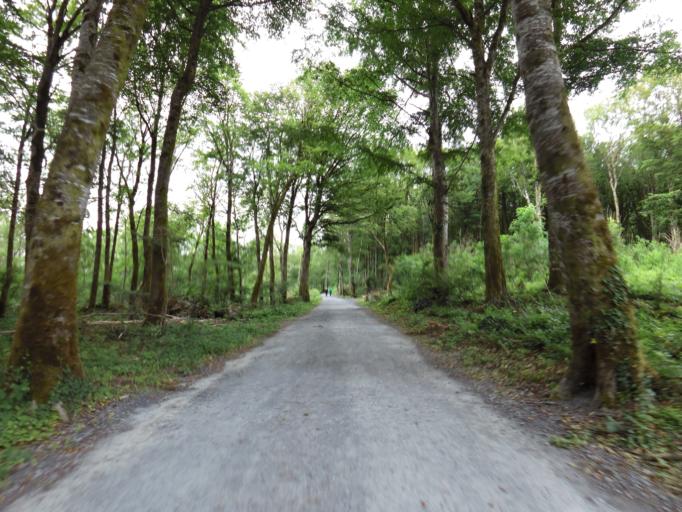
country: IE
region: Connaught
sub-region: County Galway
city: Gort
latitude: 53.0891
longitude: -8.8446
